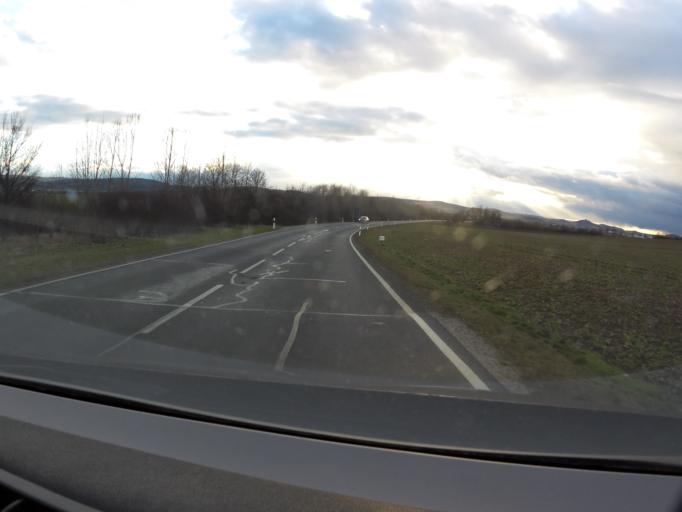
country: DE
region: Thuringia
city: Alkersleben
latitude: 50.8513
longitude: 11.0064
